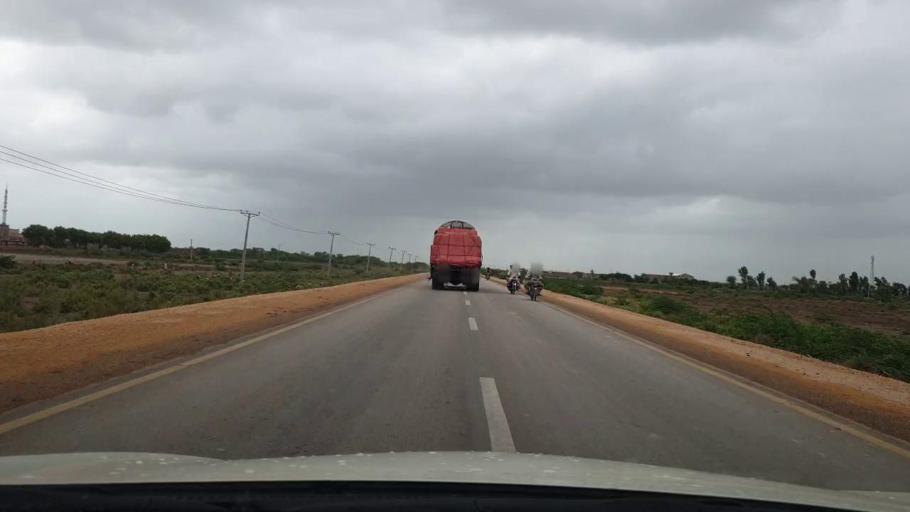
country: PK
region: Sindh
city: Badin
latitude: 24.6543
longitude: 68.7586
